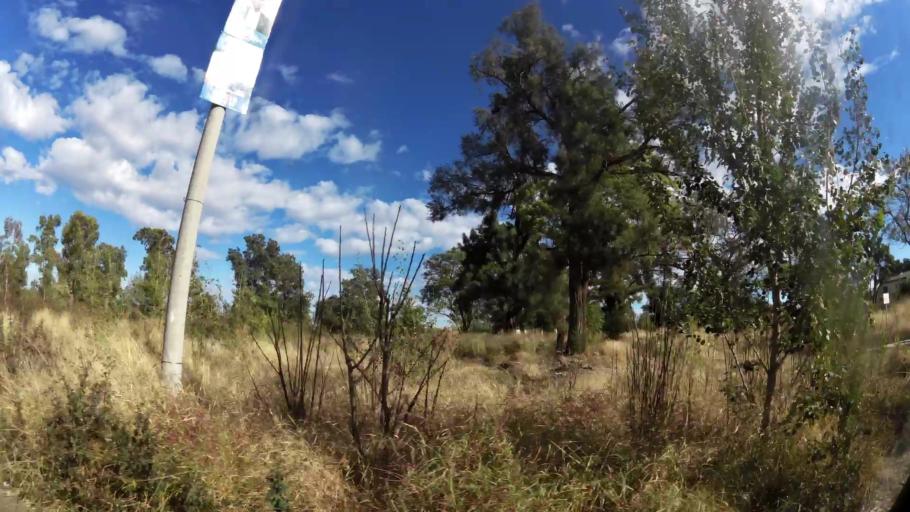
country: ZA
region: Limpopo
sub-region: Waterberg District Municipality
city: Warmbaths
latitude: -24.8806
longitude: 28.2749
